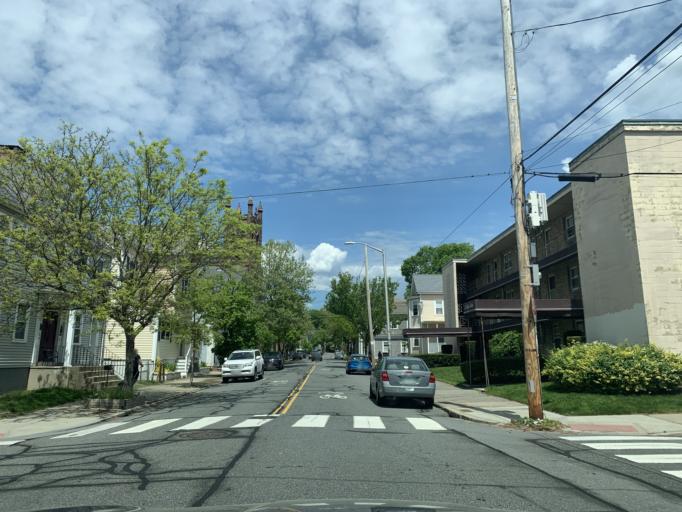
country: US
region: Rhode Island
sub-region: Providence County
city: Providence
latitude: 41.8206
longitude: -71.3959
